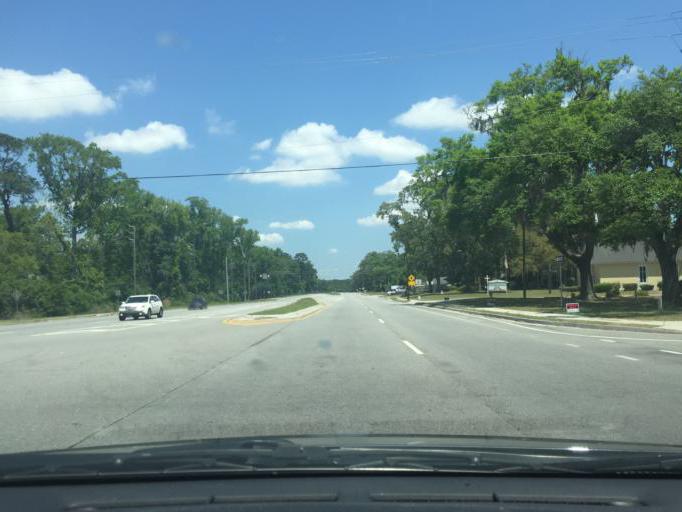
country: US
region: Georgia
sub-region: Chatham County
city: Montgomery
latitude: 31.9788
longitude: -81.1056
